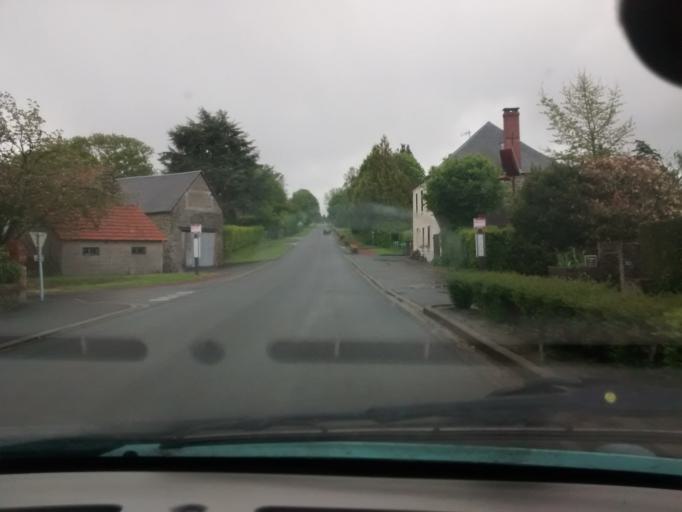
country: FR
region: Lower Normandy
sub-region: Departement de la Manche
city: Saint-Lo
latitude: 49.0940
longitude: -1.0513
